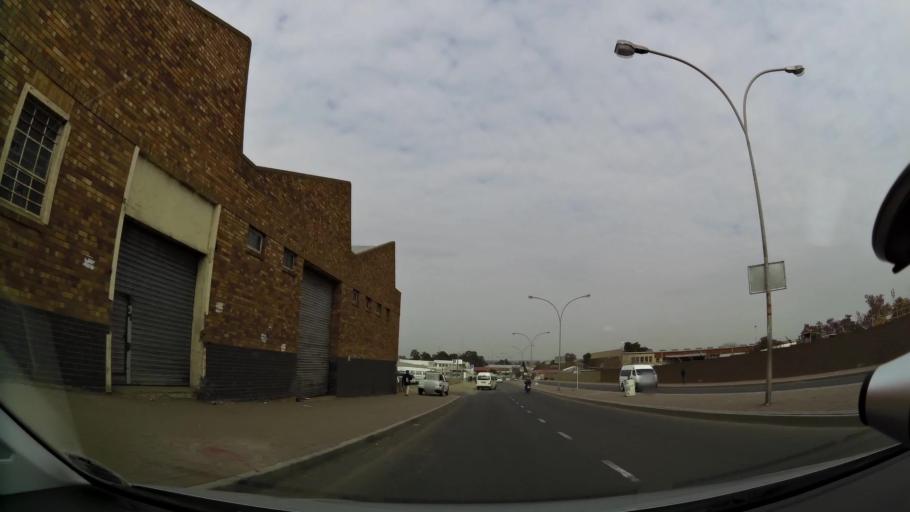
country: ZA
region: Orange Free State
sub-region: Mangaung Metropolitan Municipality
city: Bloemfontein
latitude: -29.1281
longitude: 26.2234
